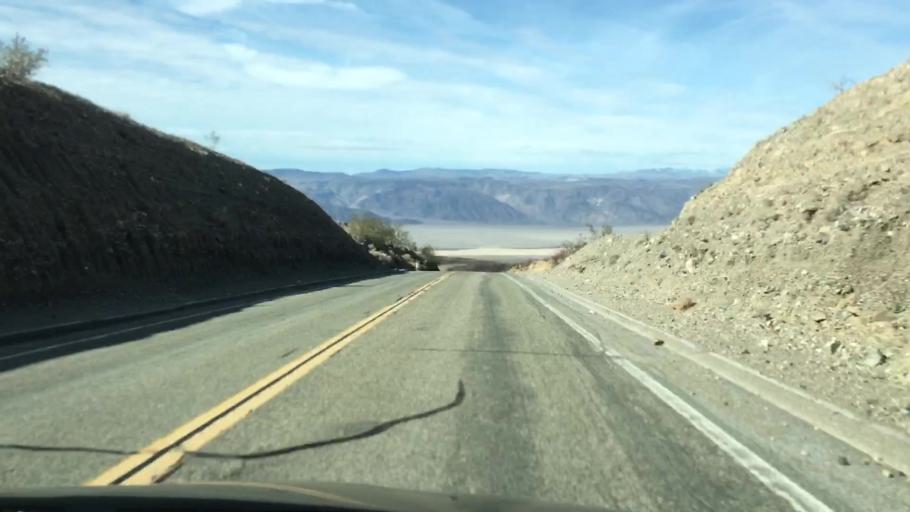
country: US
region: California
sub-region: San Bernardino County
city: Searles Valley
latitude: 36.3465
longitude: -117.3187
